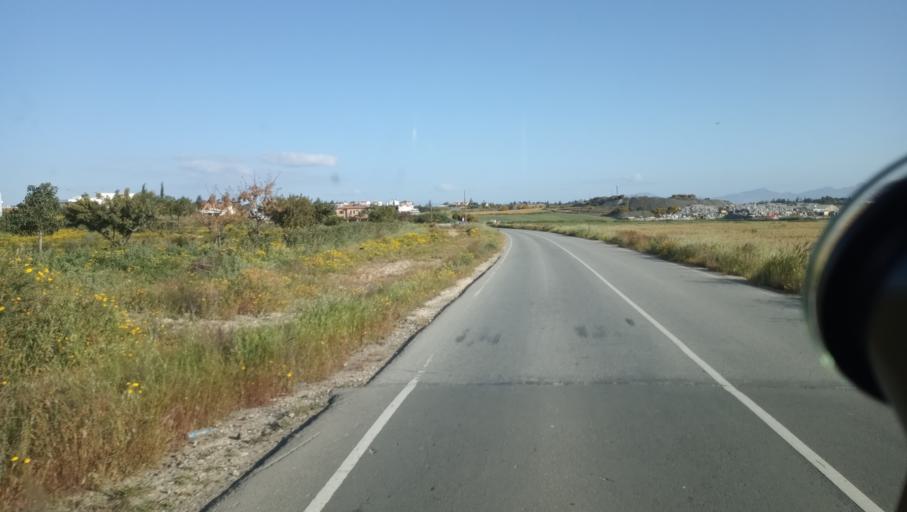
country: CY
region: Lefkosia
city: Geri
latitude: 35.0753
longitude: 33.4000
